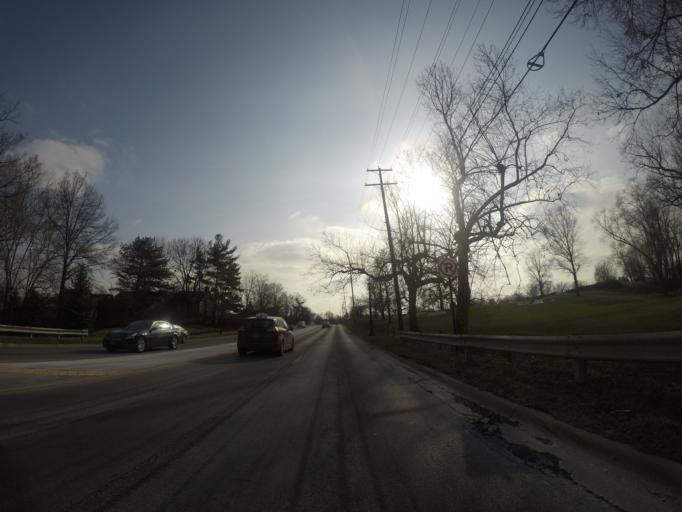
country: US
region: Ohio
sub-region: Franklin County
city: Upper Arlington
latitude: 40.0357
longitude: -83.0509
